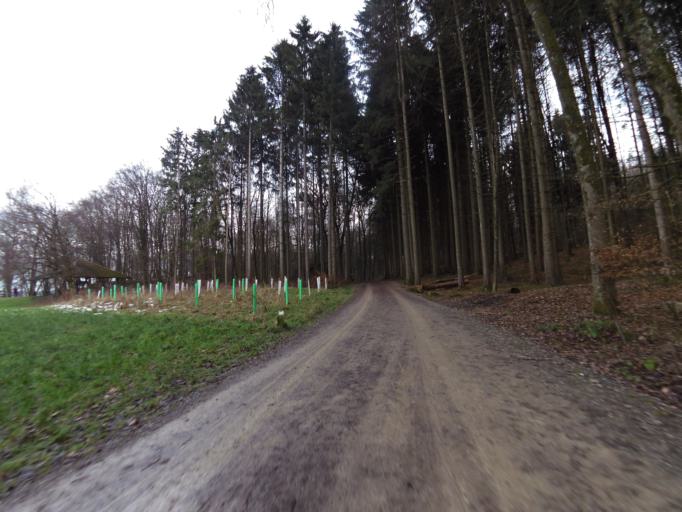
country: CH
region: Zurich
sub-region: Bezirk Dietikon
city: Schlieren / Boden
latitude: 47.3906
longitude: 8.4546
